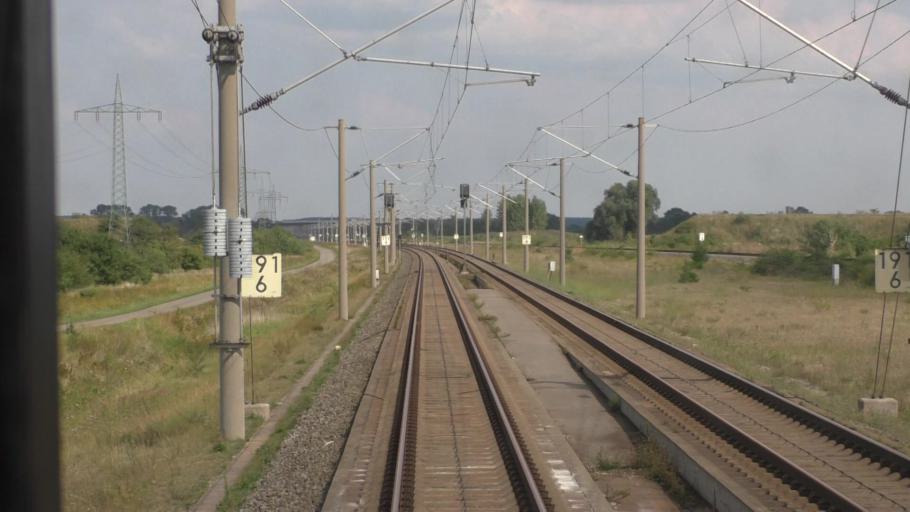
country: DE
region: Saxony-Anhalt
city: Schonhausen
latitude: 52.5906
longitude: 12.0501
